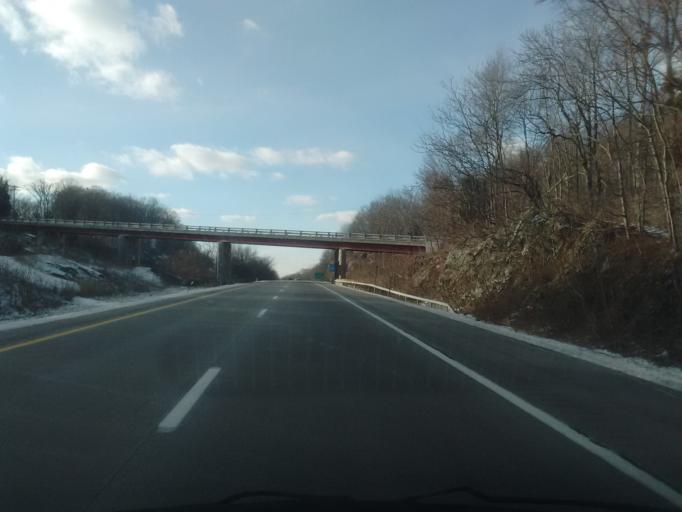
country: US
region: New York
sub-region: Dutchess County
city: Brinckerhoff
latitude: 41.5250
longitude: -73.8676
